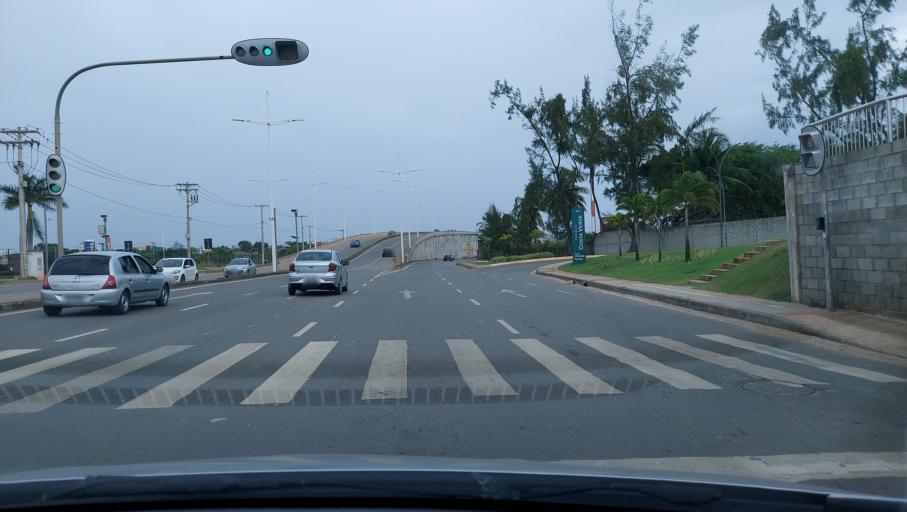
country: BR
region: Bahia
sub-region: Lauro De Freitas
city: Lauro de Freitas
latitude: -12.9458
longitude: -38.3848
